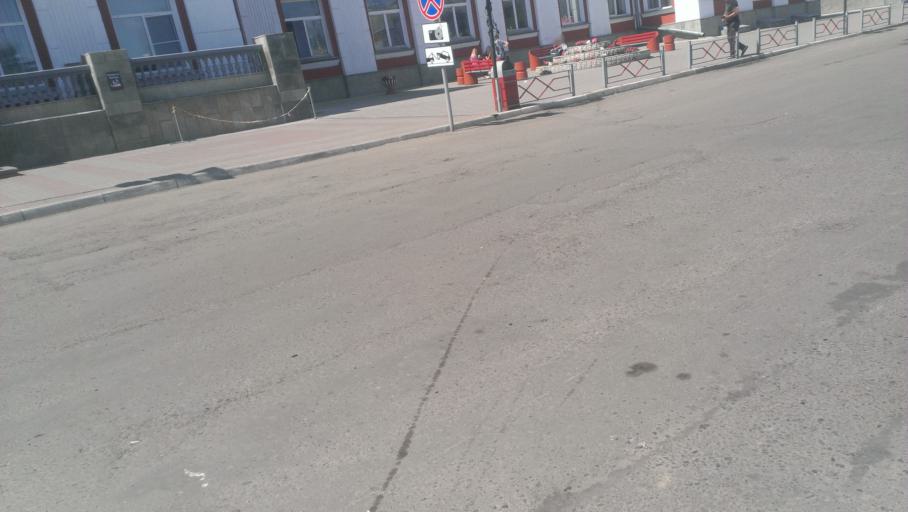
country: RU
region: Altai Krai
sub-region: Gorod Barnaulskiy
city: Barnaul
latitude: 53.3512
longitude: 83.7577
